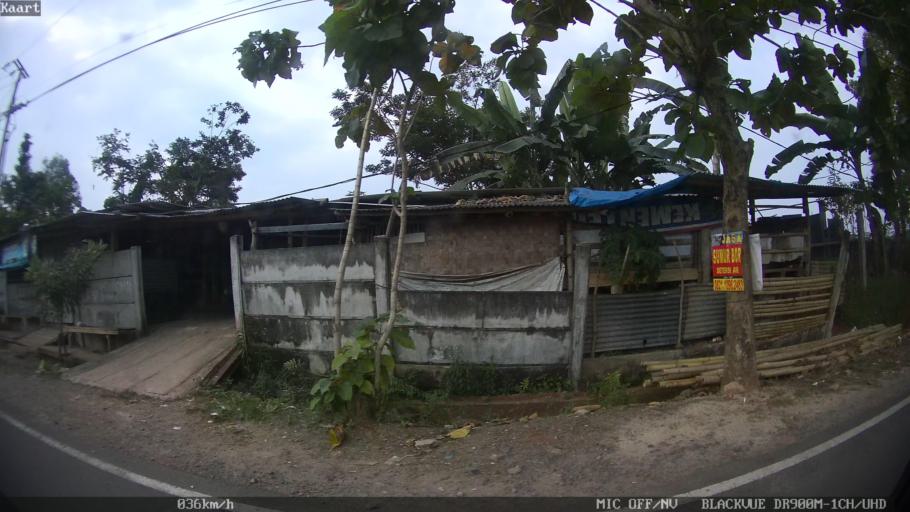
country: ID
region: Lampung
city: Bandarlampung
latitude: -5.4298
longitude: 105.2384
